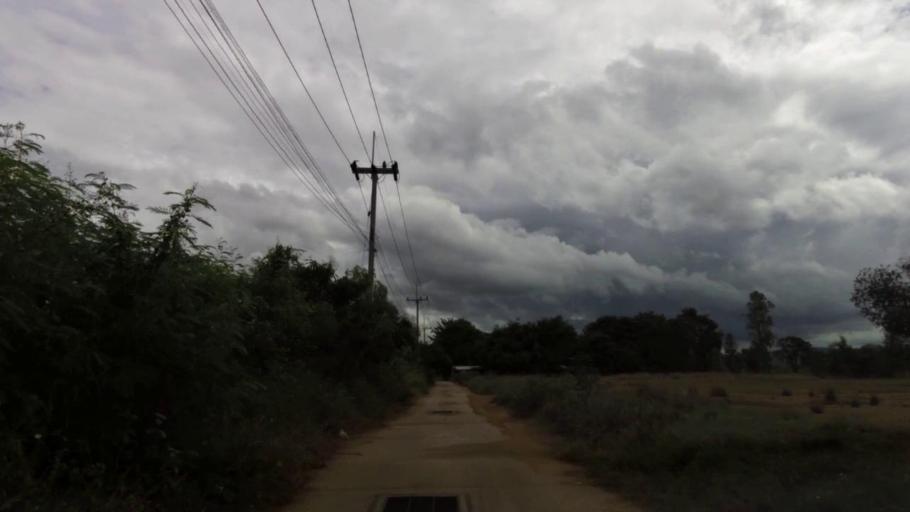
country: TH
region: Nakhon Sawan
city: Phai Sali
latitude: 15.5928
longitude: 100.6571
